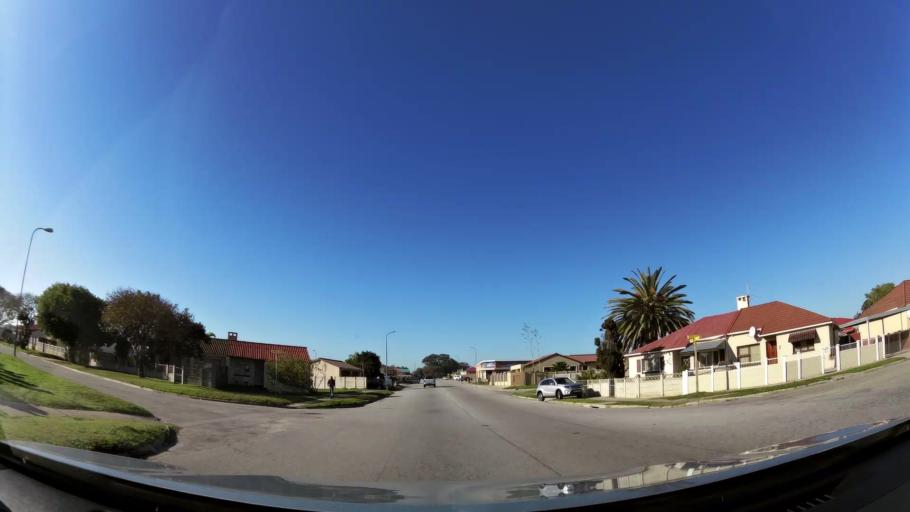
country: ZA
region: Eastern Cape
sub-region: Nelson Mandela Bay Metropolitan Municipality
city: Port Elizabeth
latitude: -33.9819
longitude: 25.6304
